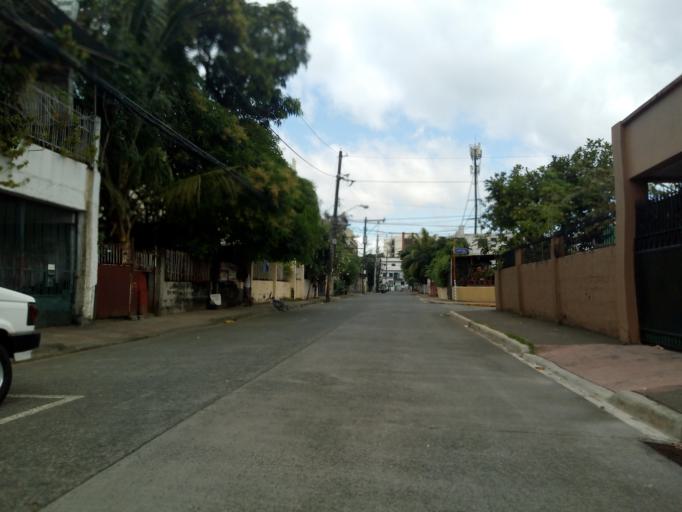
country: PH
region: Calabarzon
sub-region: Province of Rizal
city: Antipolo
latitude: 14.6385
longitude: 121.1169
